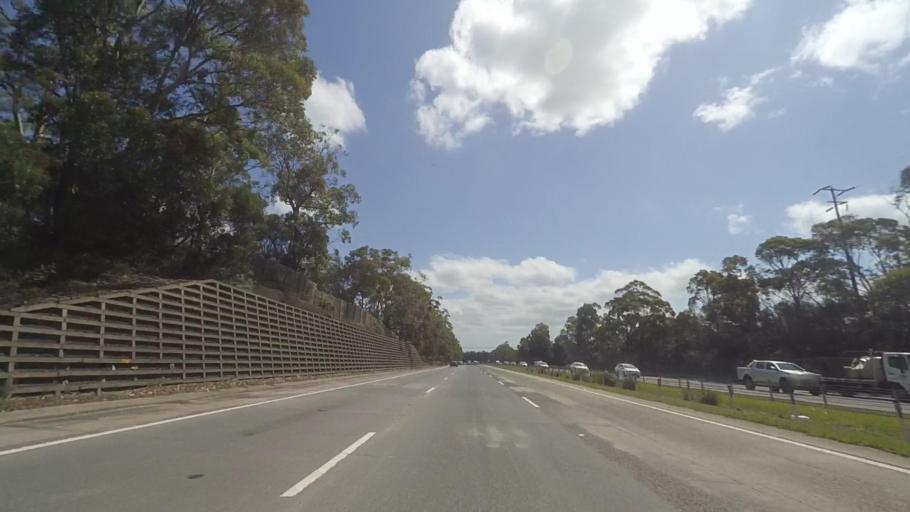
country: AU
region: New South Wales
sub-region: Hornsby Shire
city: Mount Colah
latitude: -33.6577
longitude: 151.1340
